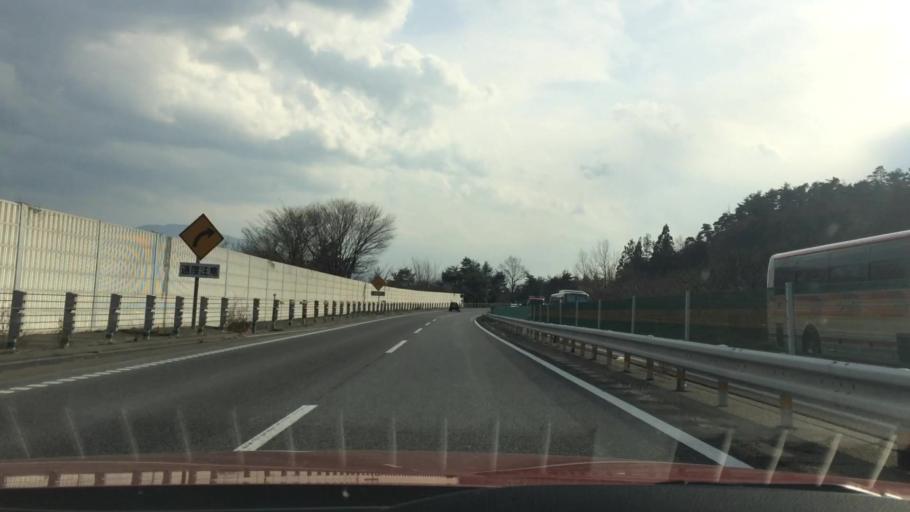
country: JP
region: Nagano
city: Ina
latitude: 35.7785
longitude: 137.9328
